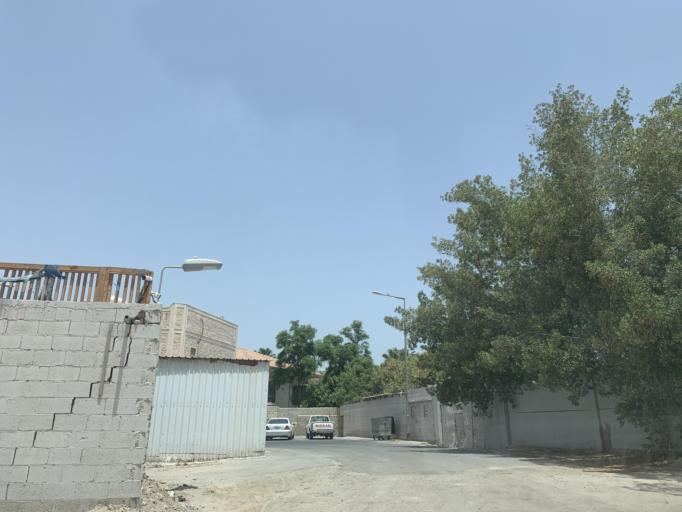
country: BH
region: Northern
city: Madinat `Isa
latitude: 26.1713
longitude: 50.5744
